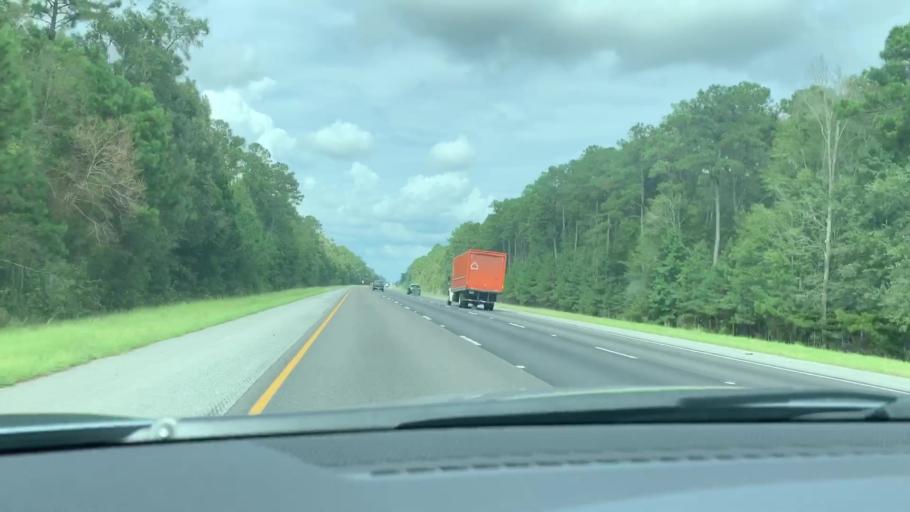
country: US
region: Georgia
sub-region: Liberty County
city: Midway
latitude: 31.7007
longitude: -81.3908
